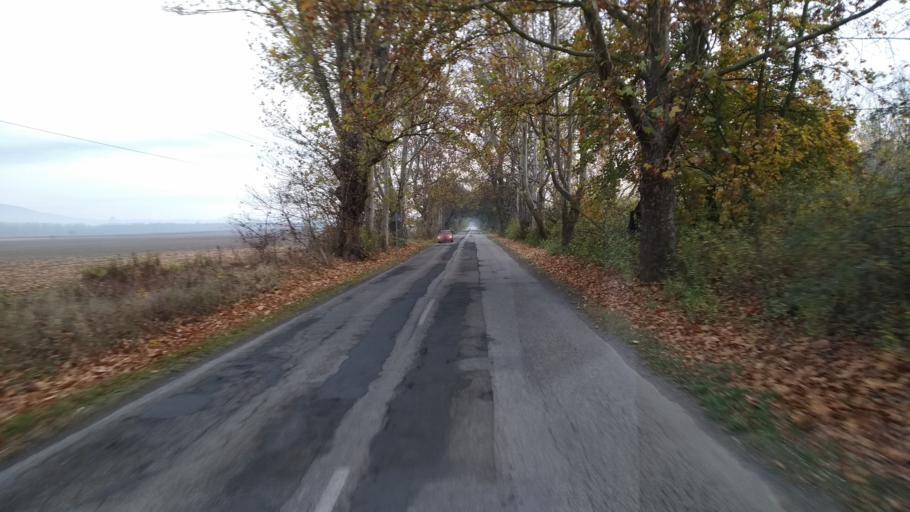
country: HU
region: Pest
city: Dunabogdany
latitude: 47.8017
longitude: 19.0359
